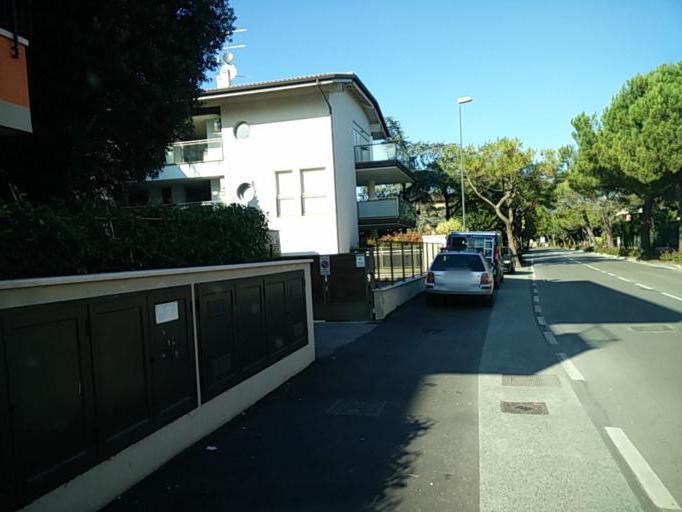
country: IT
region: Lombardy
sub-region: Provincia di Brescia
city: Sirmione
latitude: 45.4837
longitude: 10.6088
